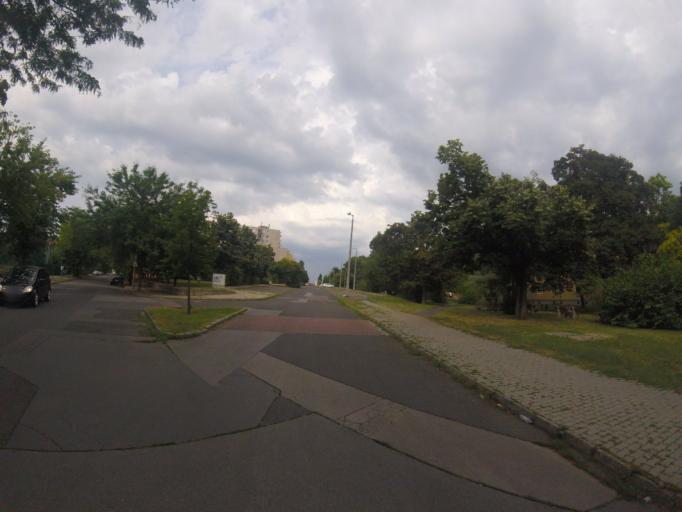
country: HU
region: Budapest
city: Budapest IV. keruelet
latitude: 47.5502
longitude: 19.0791
